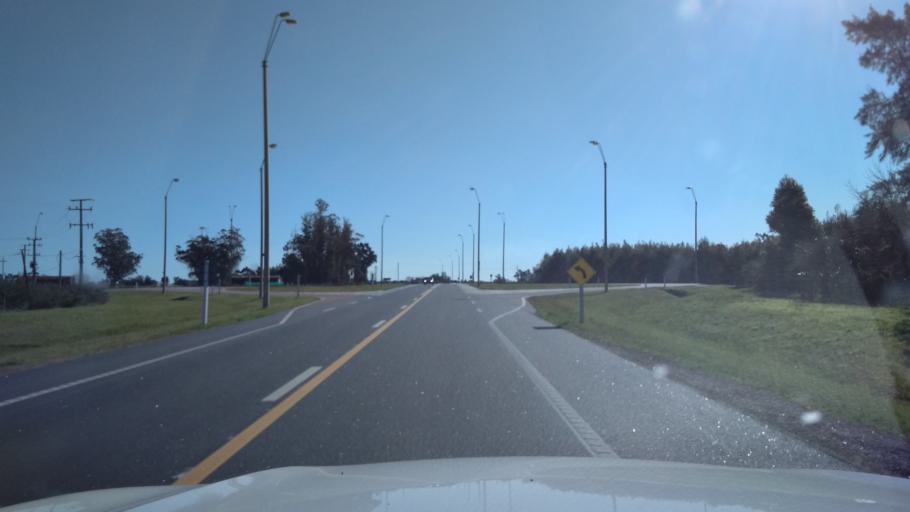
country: UY
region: Canelones
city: San Jacinto
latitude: -34.5289
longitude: -55.9513
